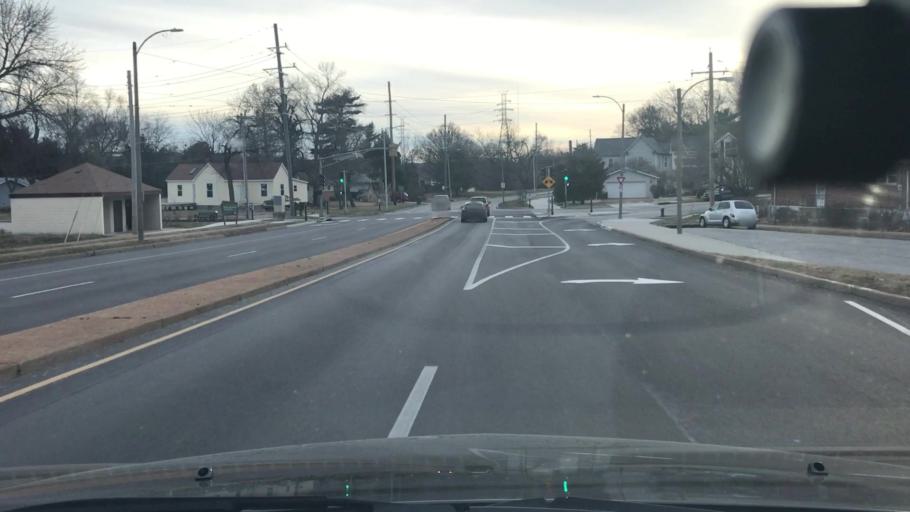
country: US
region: Missouri
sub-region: Saint Louis County
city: Maplewood
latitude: 38.6091
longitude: -90.3112
